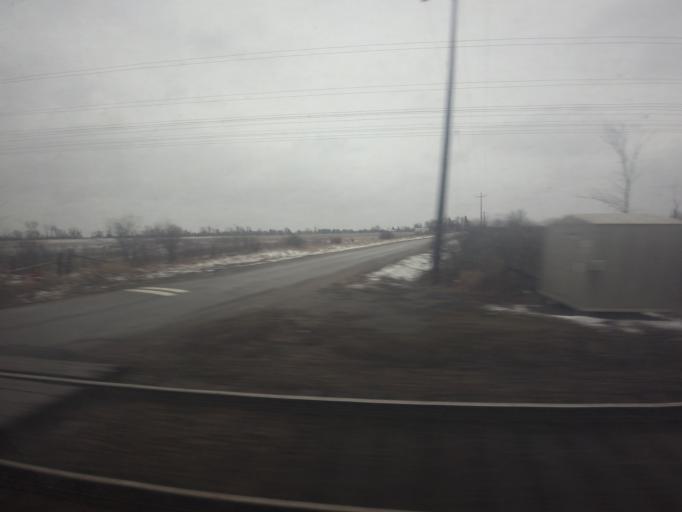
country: CA
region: Ontario
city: Gananoque
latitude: 44.3345
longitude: -76.3040
